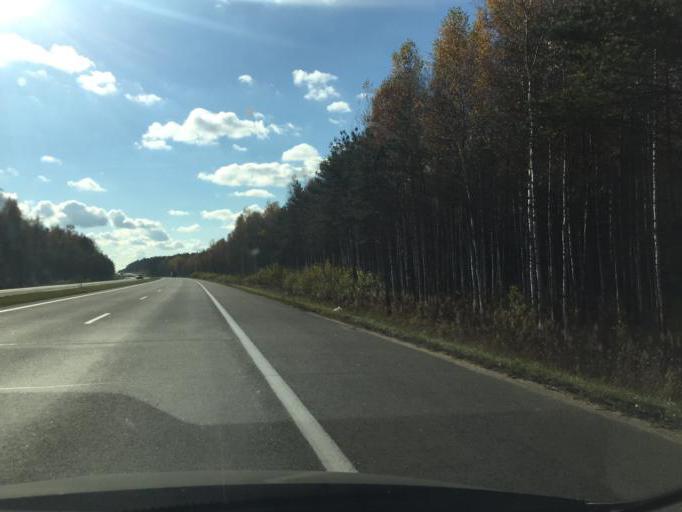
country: BY
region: Minsk
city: Slabada
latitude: 53.9376
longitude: 27.9636
